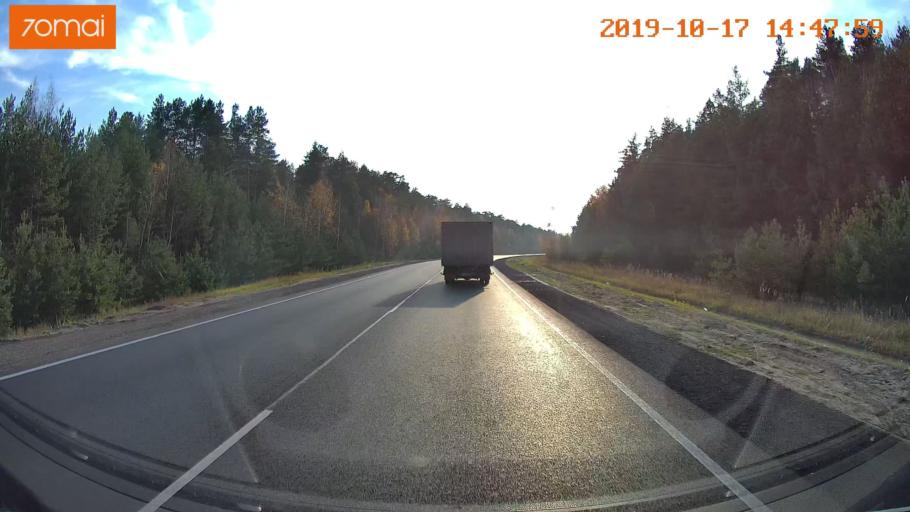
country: RU
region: Rjazan
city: Solotcha
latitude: 54.7641
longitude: 39.8551
